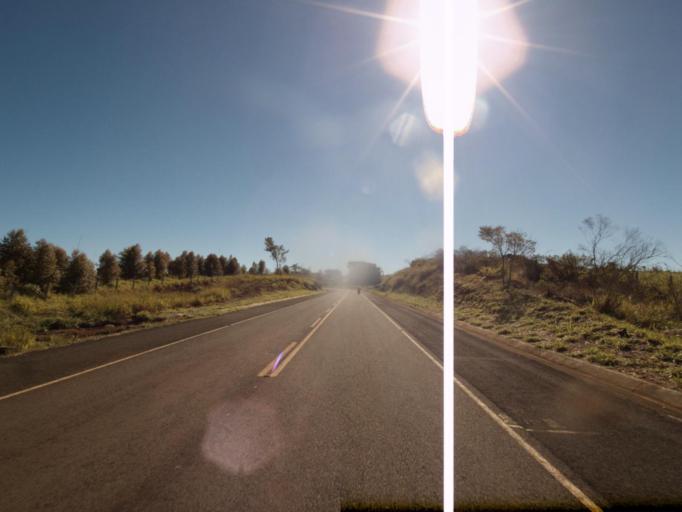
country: AR
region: Misiones
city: Bernardo de Irigoyen
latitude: -26.6117
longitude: -53.6886
